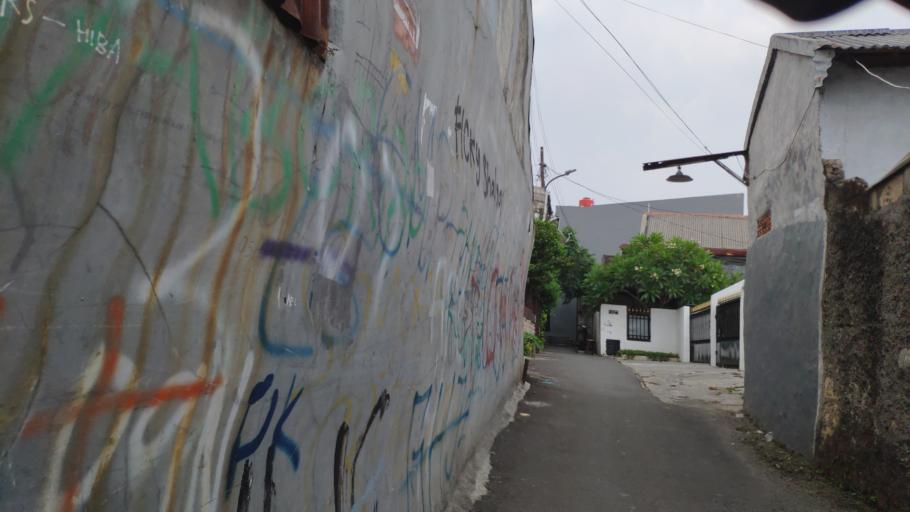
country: ID
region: Jakarta Raya
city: Jakarta
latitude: -6.2632
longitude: 106.7937
